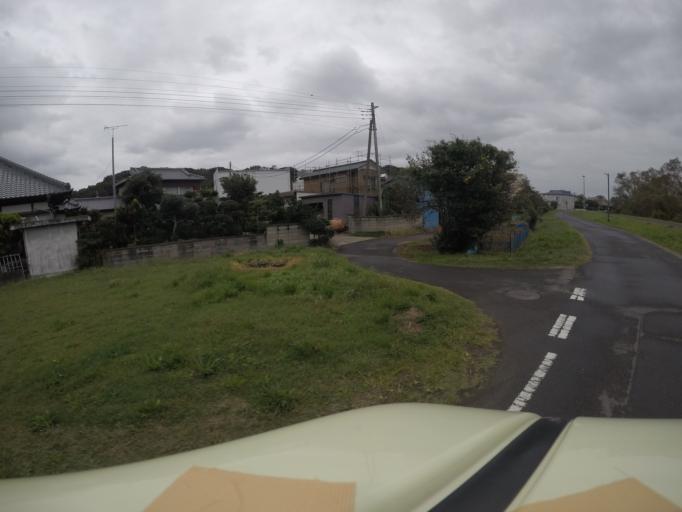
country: JP
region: Ibaraki
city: Itako
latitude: 35.9988
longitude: 140.4709
